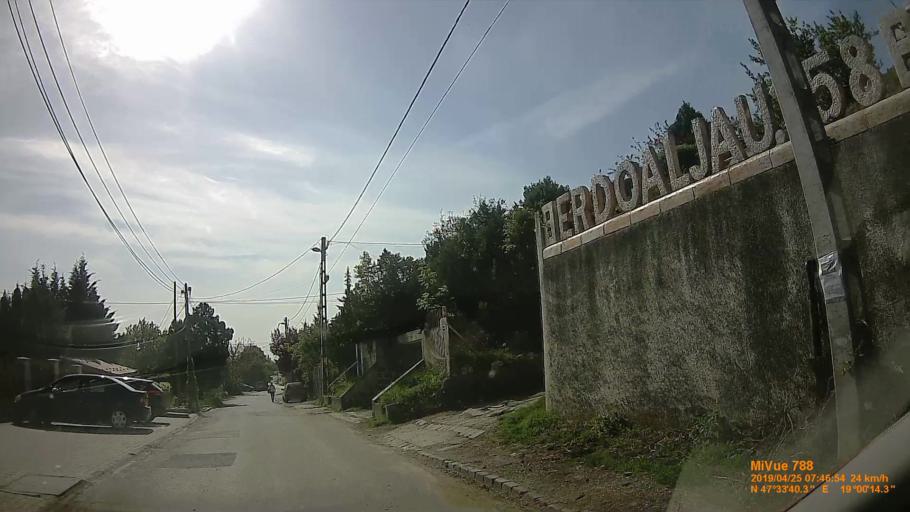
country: HU
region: Pest
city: Urom
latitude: 47.5612
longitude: 19.0040
